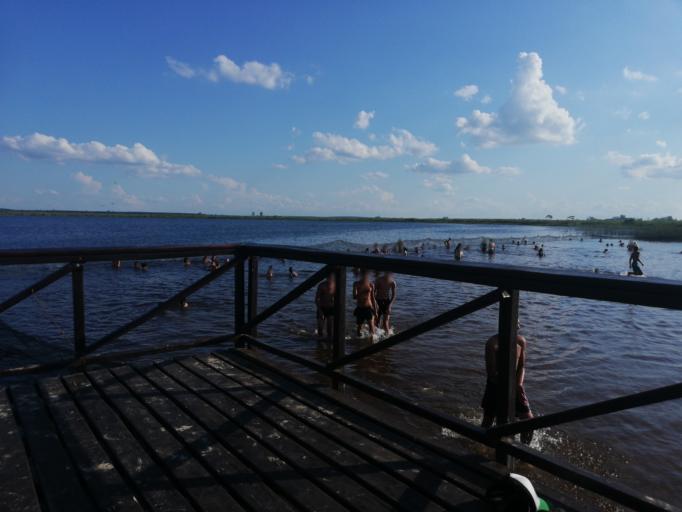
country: AR
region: Corrientes
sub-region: Departamento de San Miguel
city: San Miguel
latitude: -28.0062
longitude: -57.5924
